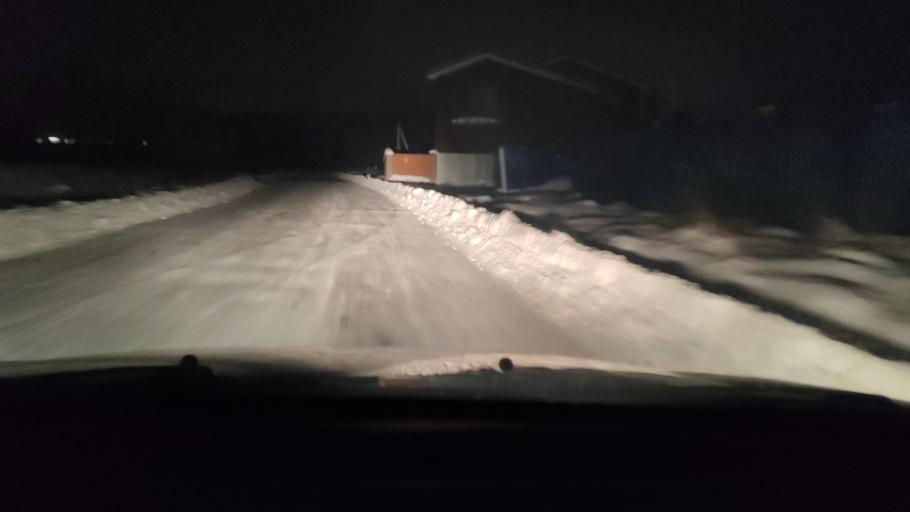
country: RU
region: Perm
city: Perm
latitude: 57.9953
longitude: 56.3414
